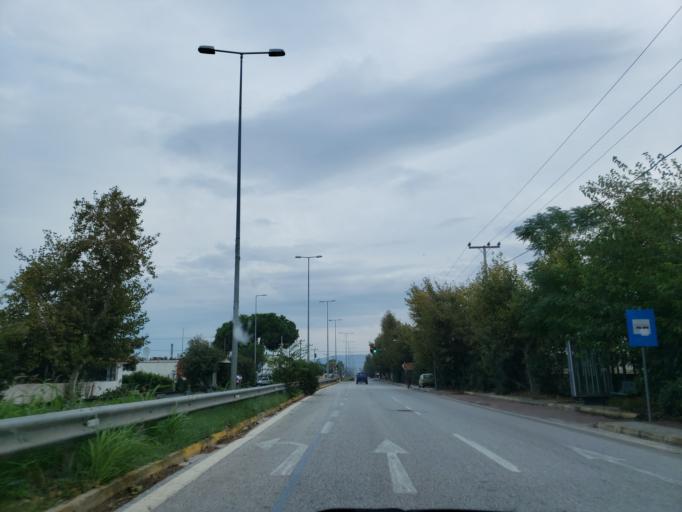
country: GR
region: Attica
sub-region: Nomarchia Anatolikis Attikis
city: Aghios Panteleimon
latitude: 38.1172
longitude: 23.9698
